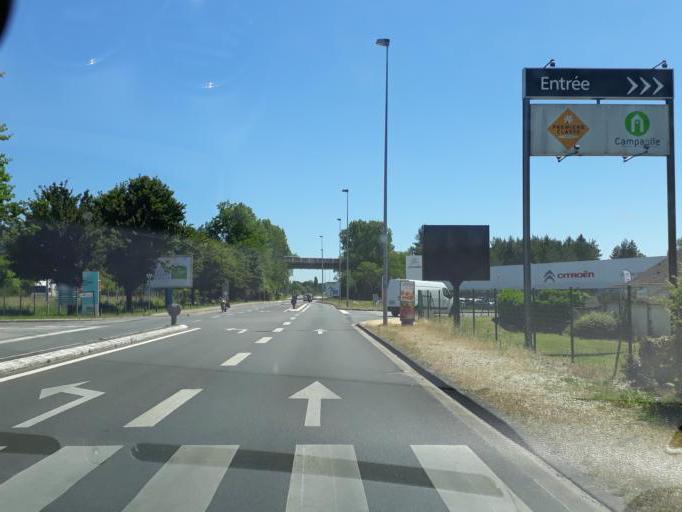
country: FR
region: Centre
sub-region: Departement du Cher
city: Vierzon
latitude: 47.2151
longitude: 2.1109
